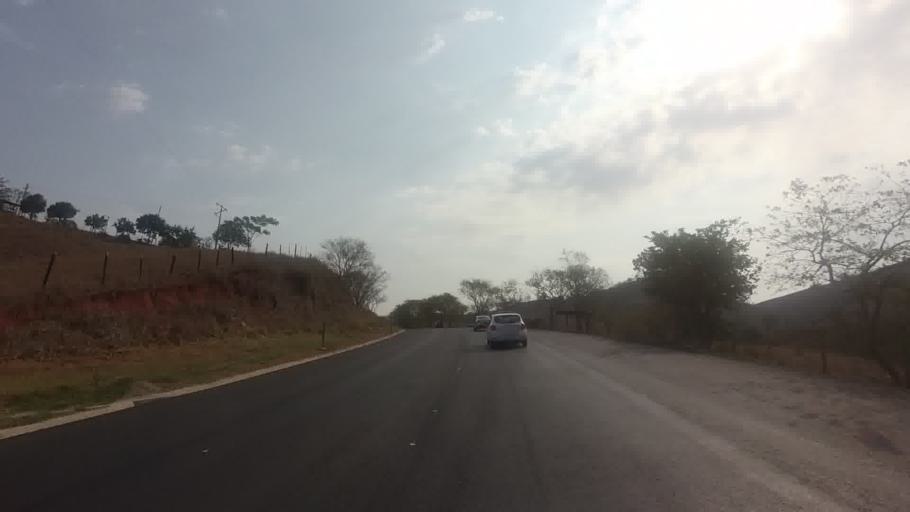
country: BR
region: Rio de Janeiro
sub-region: Bom Jesus Do Itabapoana
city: Bom Jesus do Itabapoana
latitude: -21.1951
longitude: -41.7074
